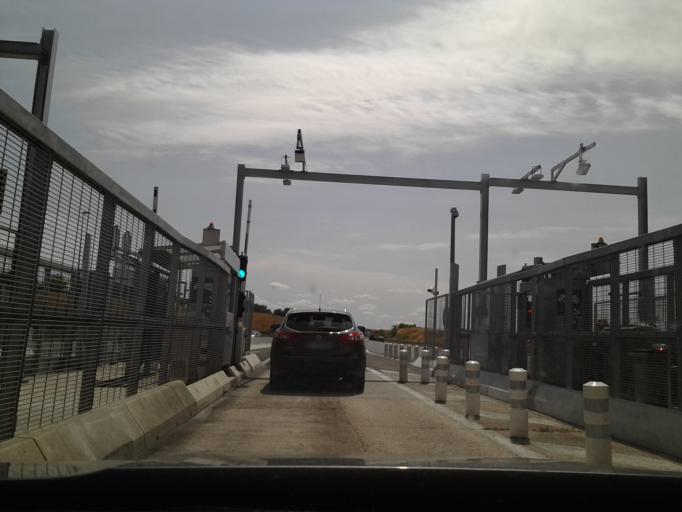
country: FR
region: Centre
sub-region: Departement d'Indre-et-Loire
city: Saint-Christophe-sur-le-Nais
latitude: 47.6382
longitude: 0.4969
